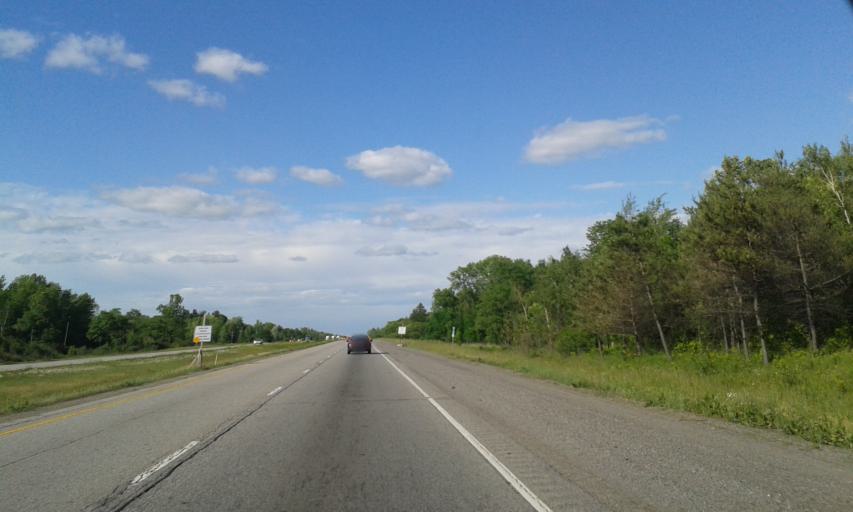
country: CA
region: Ontario
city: Prescott
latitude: 44.6745
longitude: -75.6000
